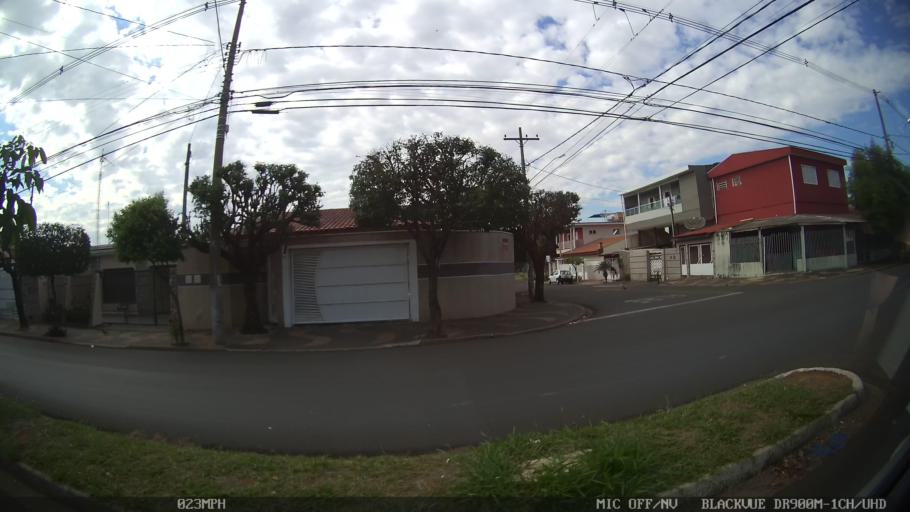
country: BR
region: Sao Paulo
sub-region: Americana
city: Americana
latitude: -22.7404
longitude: -47.3645
